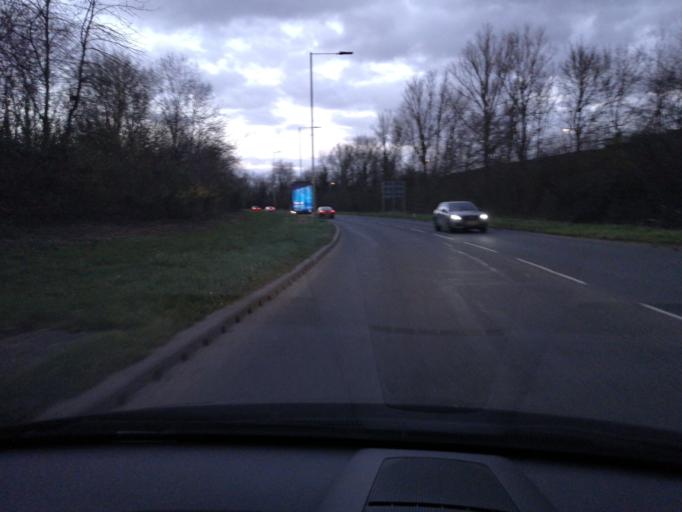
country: GB
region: England
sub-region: Peterborough
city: Eye
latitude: 52.5934
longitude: -0.2039
